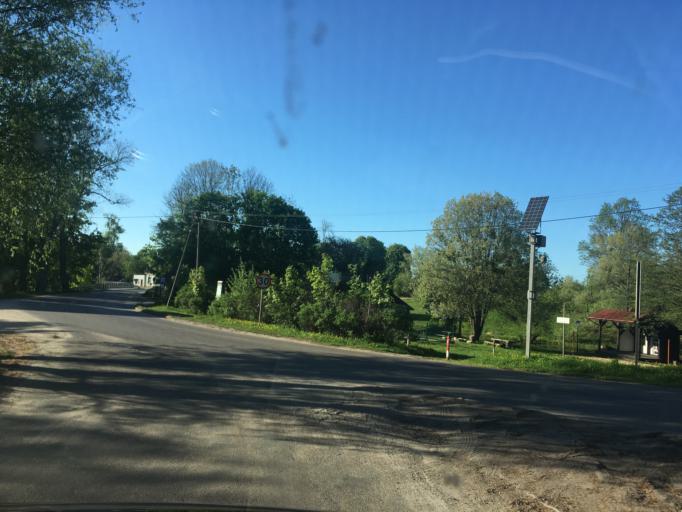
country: PL
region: Warmian-Masurian Voivodeship
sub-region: Powiat piski
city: Ruciane-Nida
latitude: 53.6872
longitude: 21.5000
